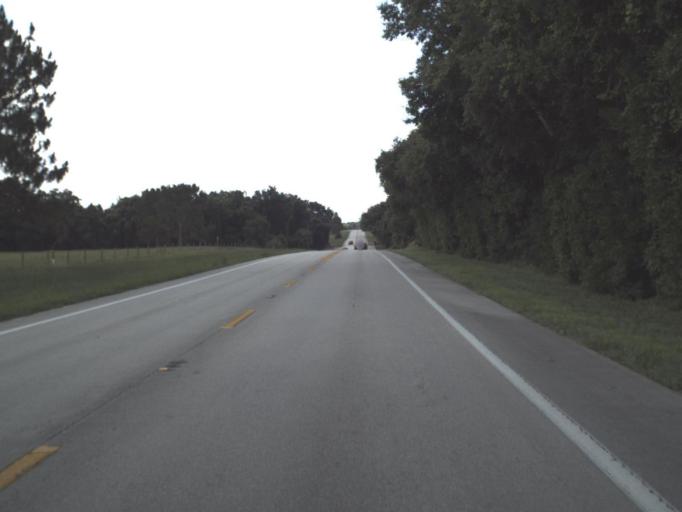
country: US
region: Florida
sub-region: Putnam County
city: Palatka
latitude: 29.5443
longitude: -81.6502
